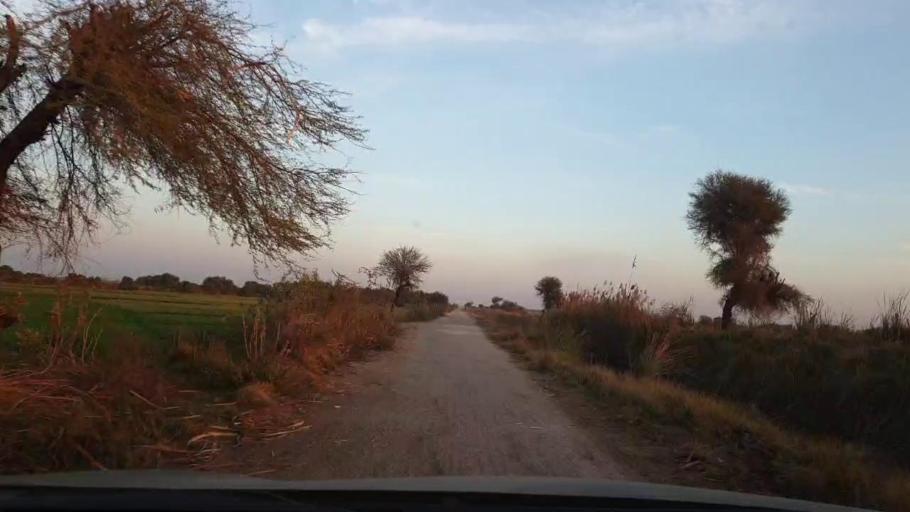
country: PK
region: Sindh
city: Tando Allahyar
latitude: 25.5862
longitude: 68.7188
